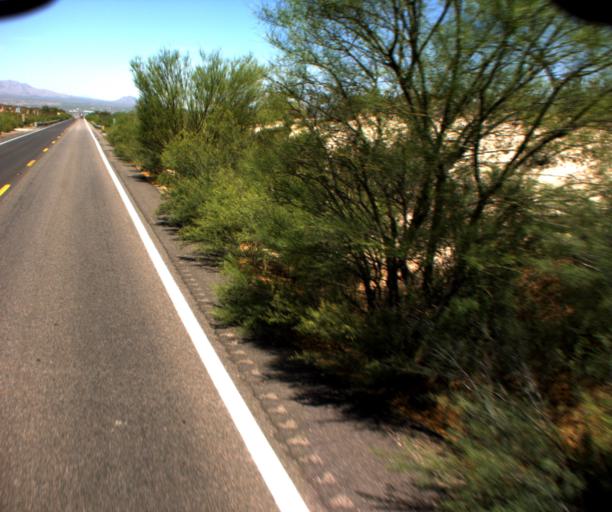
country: US
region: Arizona
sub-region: Gila County
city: Peridot
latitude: 33.2899
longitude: -110.4099
